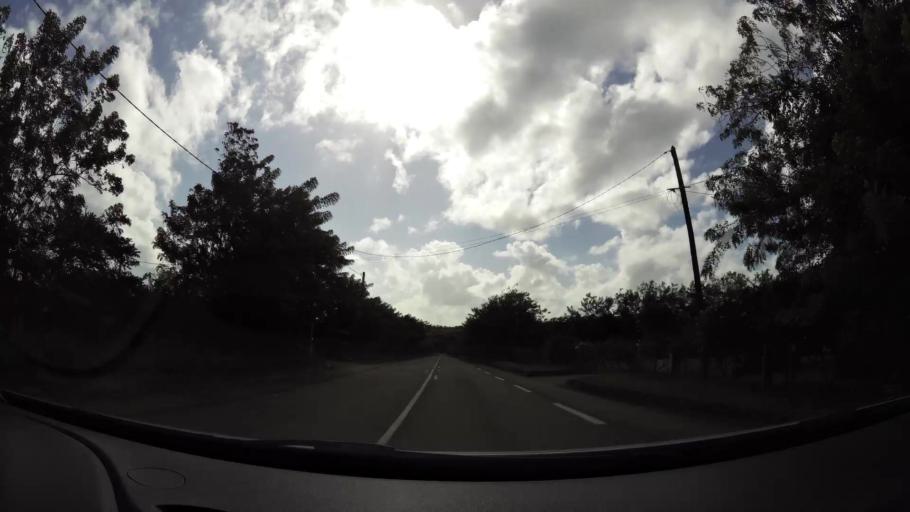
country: MQ
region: Martinique
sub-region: Martinique
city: Le Vauclin
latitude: 14.5745
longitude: -60.8639
